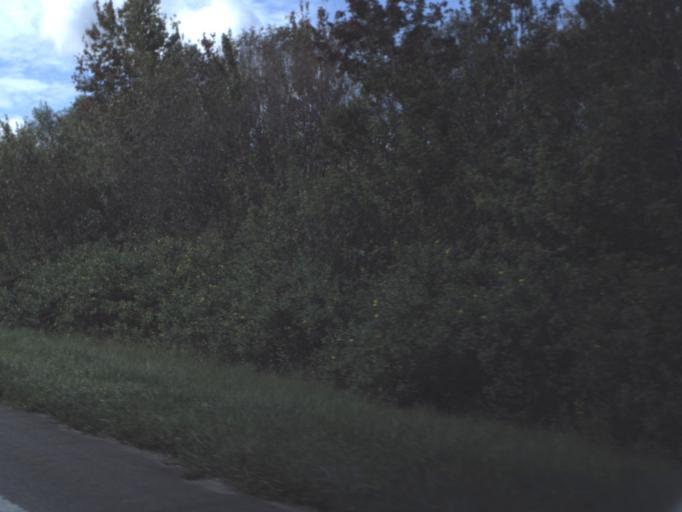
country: US
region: Florida
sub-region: Collier County
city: Orangetree
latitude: 26.0883
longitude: -81.3447
